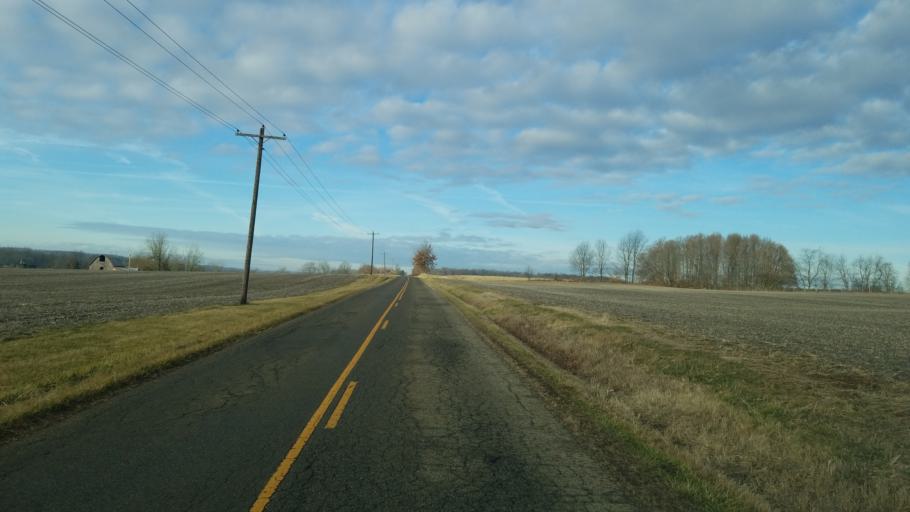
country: US
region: Ohio
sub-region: Knox County
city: Gambier
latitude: 40.3137
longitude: -82.3379
